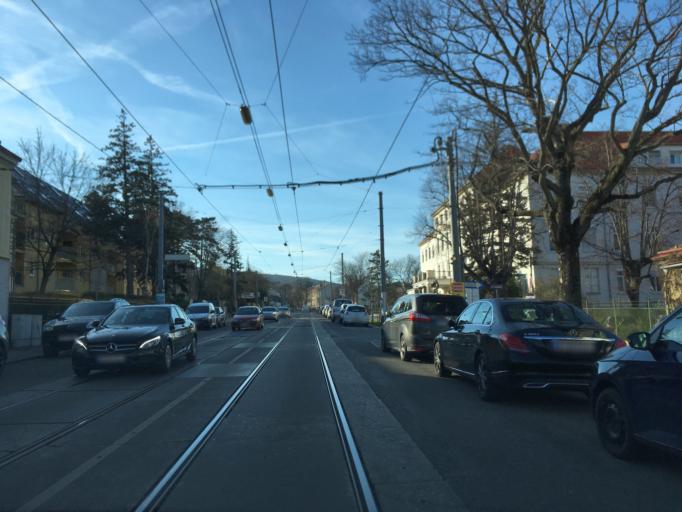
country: AT
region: Vienna
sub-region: Wien Stadt
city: Vienna
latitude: 48.2272
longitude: 16.3053
